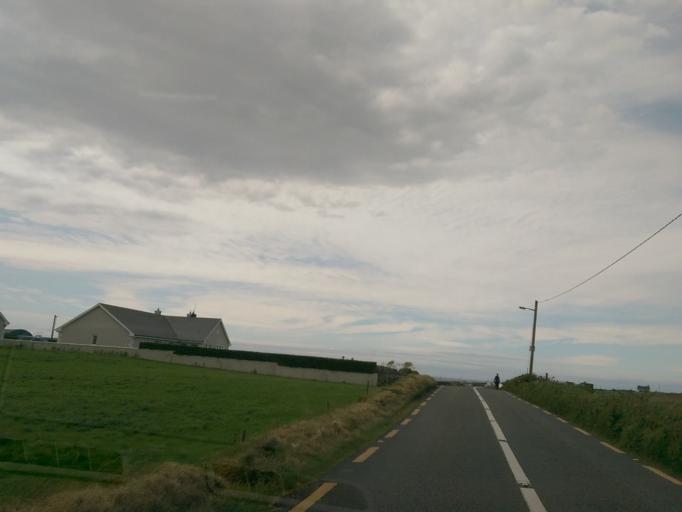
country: IE
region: Munster
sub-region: An Clar
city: Kilrush
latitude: 52.8615
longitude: -9.4086
